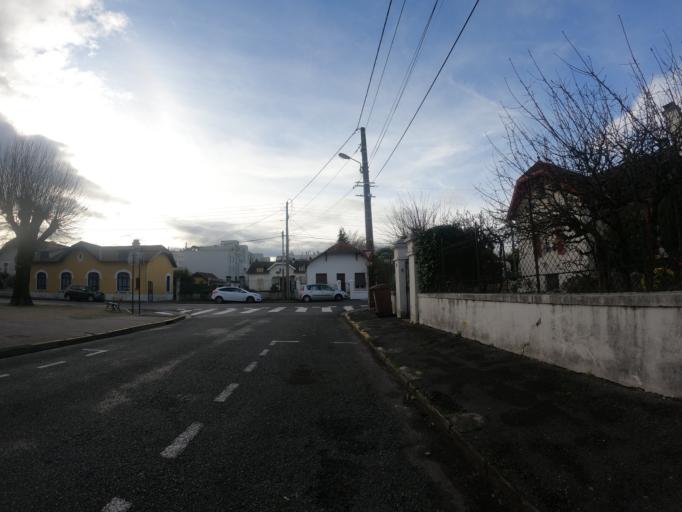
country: FR
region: Aquitaine
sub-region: Departement des Pyrenees-Atlantiques
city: Jurancon
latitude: 43.2908
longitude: -0.3805
